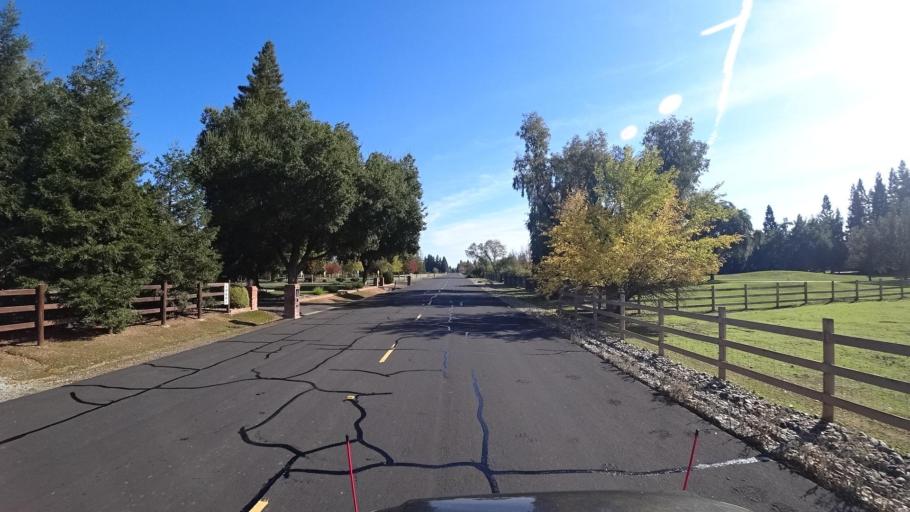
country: US
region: California
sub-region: Sacramento County
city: Wilton
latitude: 38.4363
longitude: -121.2904
